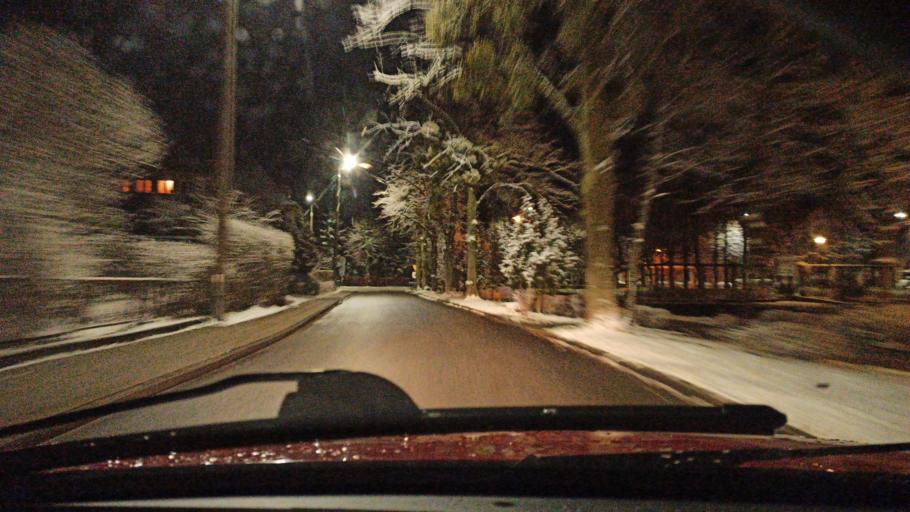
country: PL
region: Warmian-Masurian Voivodeship
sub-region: Powiat elblaski
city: Elblag
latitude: 54.1734
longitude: 19.4076
